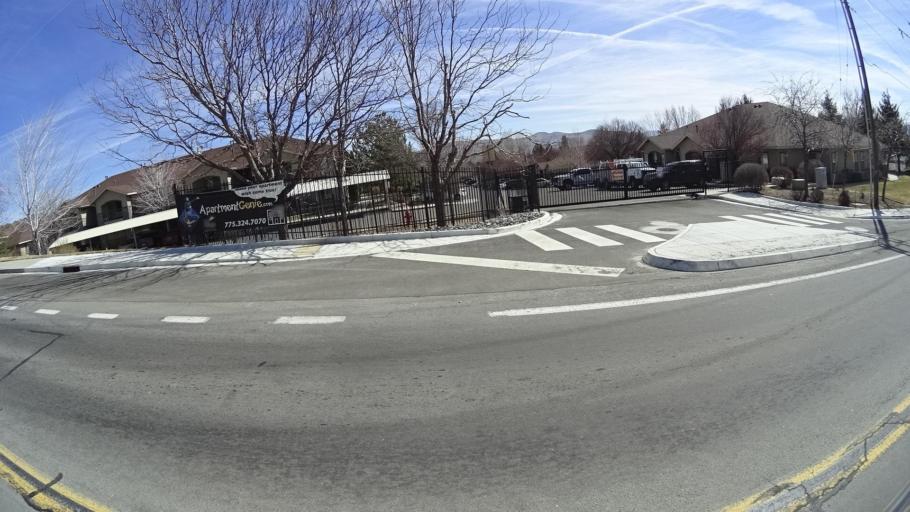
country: US
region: Nevada
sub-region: Washoe County
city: Sparks
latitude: 39.5550
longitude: -119.7712
